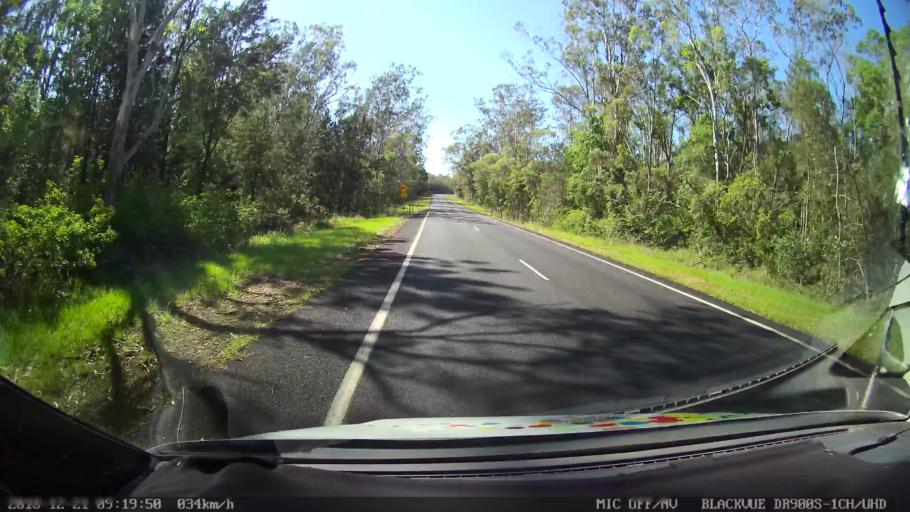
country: AU
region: New South Wales
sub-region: Clarence Valley
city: Maclean
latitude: -29.3095
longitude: 152.9975
